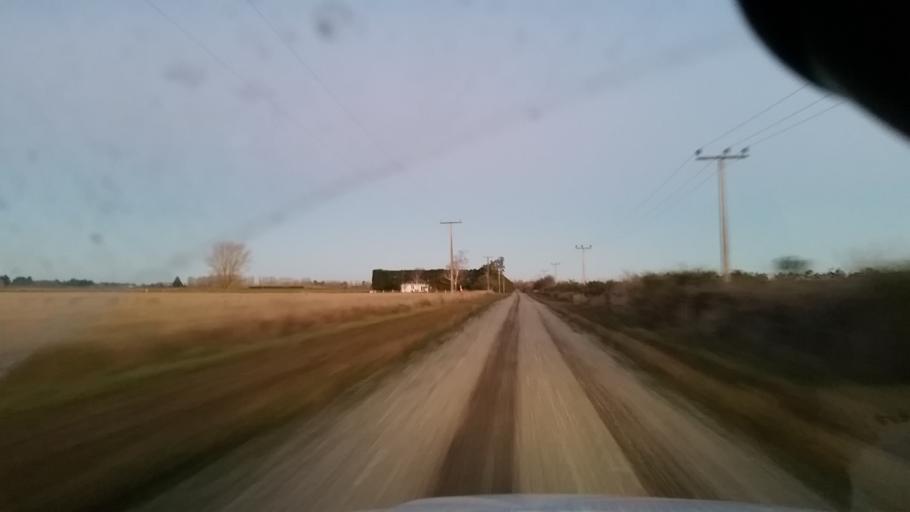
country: NZ
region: Canterbury
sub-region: Ashburton District
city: Tinwald
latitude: -43.9956
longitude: 171.6620
